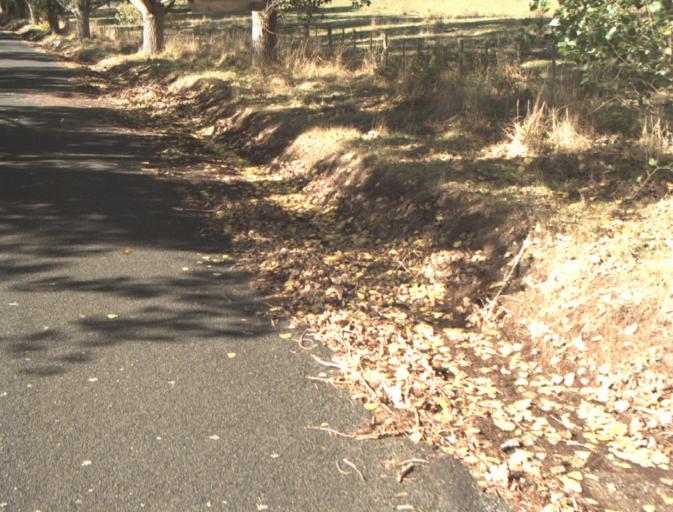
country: AU
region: Tasmania
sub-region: Launceston
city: Mayfield
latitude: -41.2893
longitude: 147.2087
